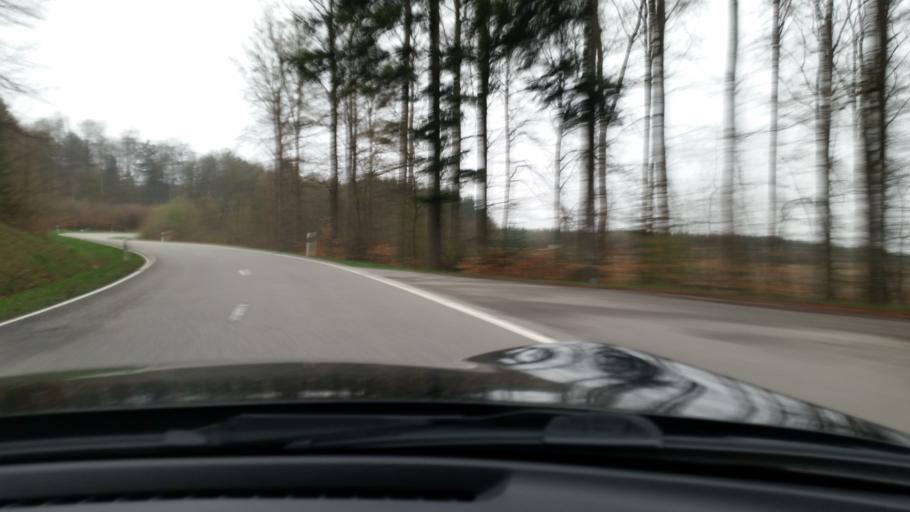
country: DE
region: Baden-Wuerttemberg
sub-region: Karlsruhe Region
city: Walldurn
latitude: 49.5514
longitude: 9.3839
